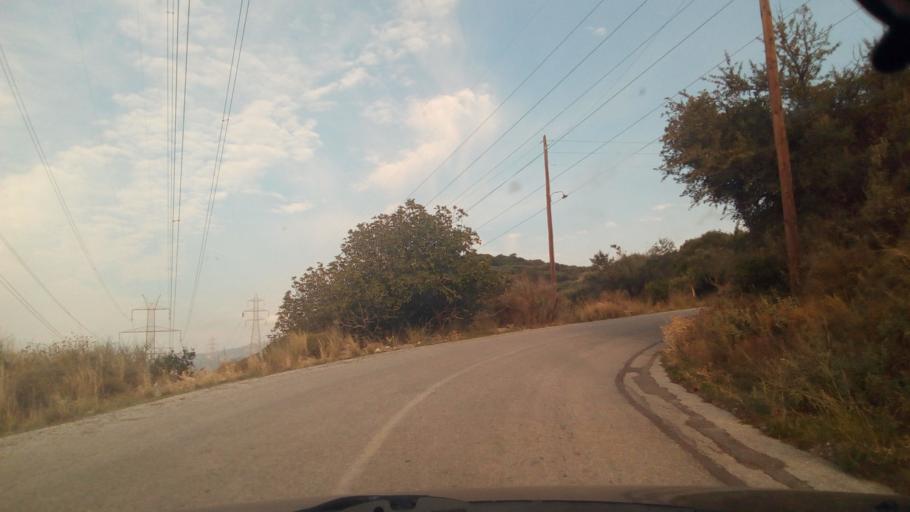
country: GR
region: West Greece
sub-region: Nomos Aitolias kai Akarnanias
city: Nafpaktos
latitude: 38.4134
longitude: 21.9262
